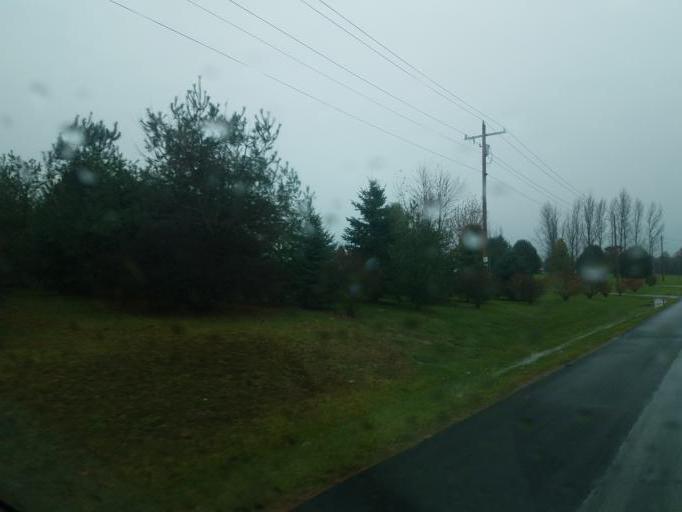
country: US
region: Ohio
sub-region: Knox County
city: Centerburg
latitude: 40.2913
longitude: -82.7311
